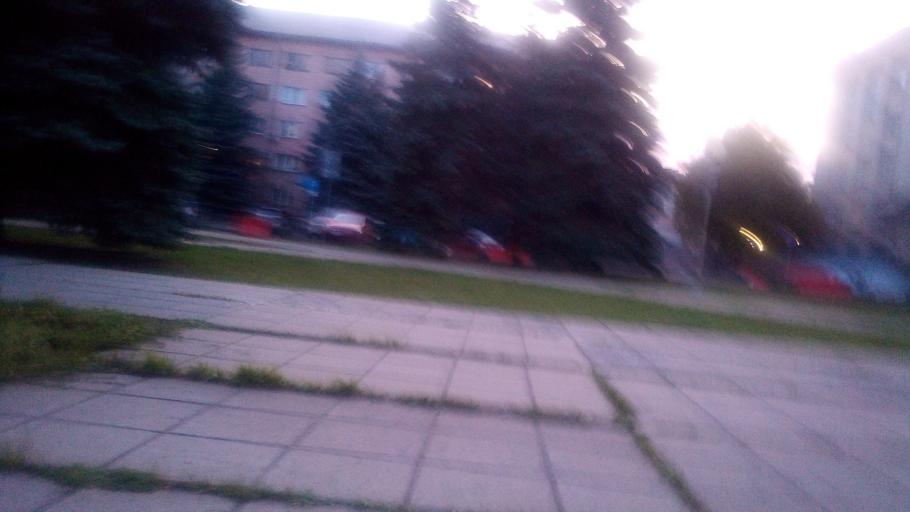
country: RU
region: Chelyabinsk
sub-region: Gorod Chelyabinsk
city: Chelyabinsk
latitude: 55.1585
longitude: 61.3705
